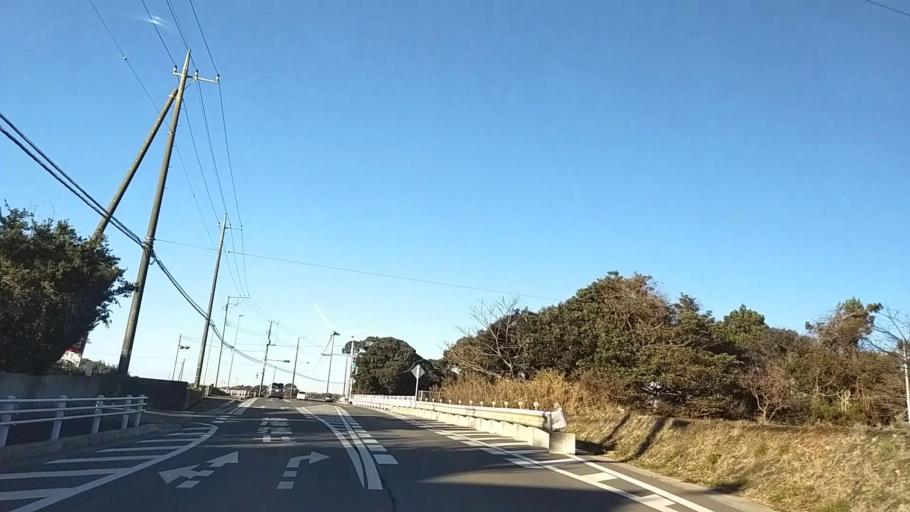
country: JP
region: Chiba
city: Hasaki
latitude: 35.7516
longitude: 140.7398
